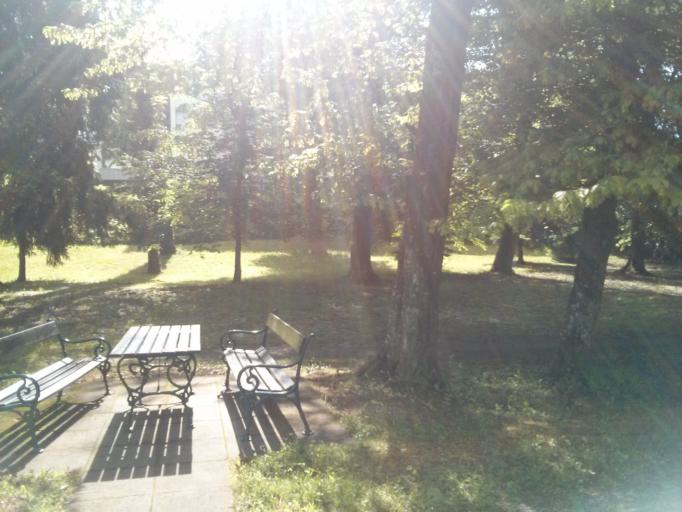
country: AT
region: Burgenland
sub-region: Politischer Bezirk Oberwart
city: Bad Tatzmannsdorf
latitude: 47.3341
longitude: 16.2295
